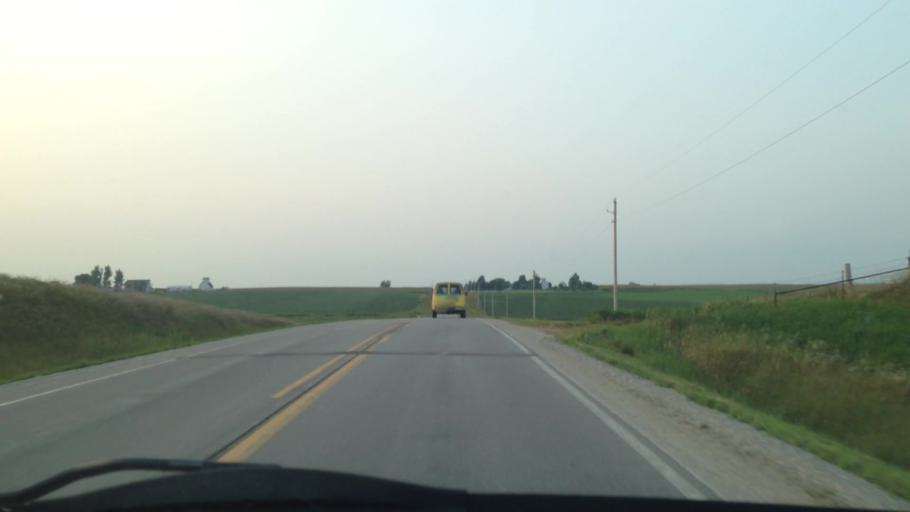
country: US
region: Iowa
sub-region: Benton County
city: Atkins
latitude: 42.0141
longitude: -91.8737
